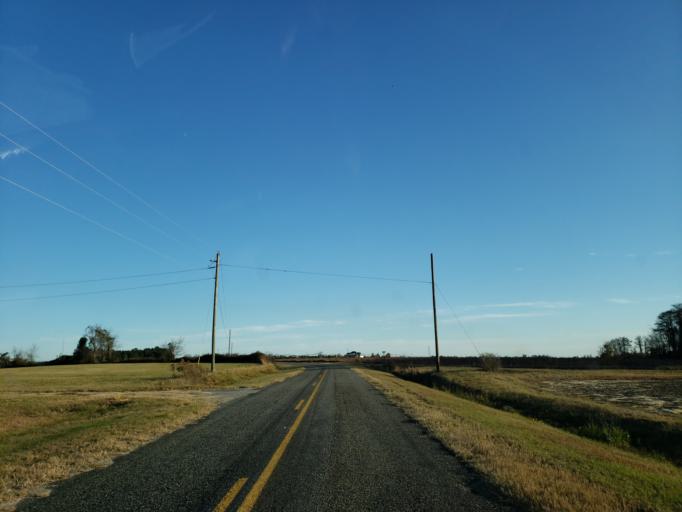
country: US
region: Georgia
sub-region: Dooly County
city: Unadilla
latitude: 32.1918
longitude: -83.7820
